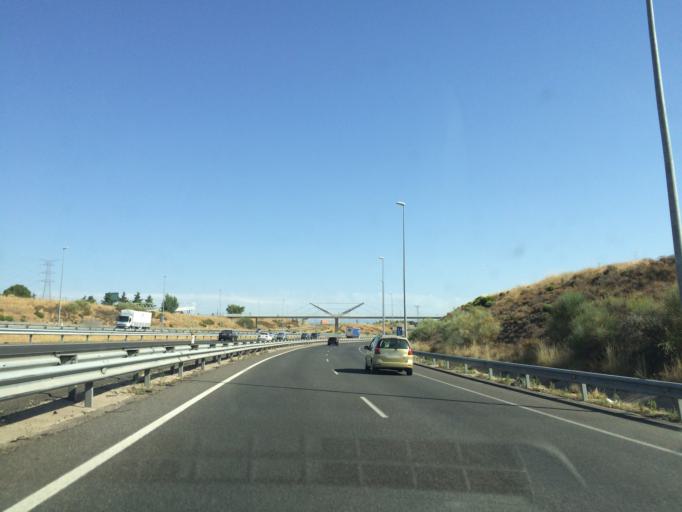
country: ES
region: Madrid
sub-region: Provincia de Madrid
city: Majadahonda
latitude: 40.4460
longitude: -3.8793
